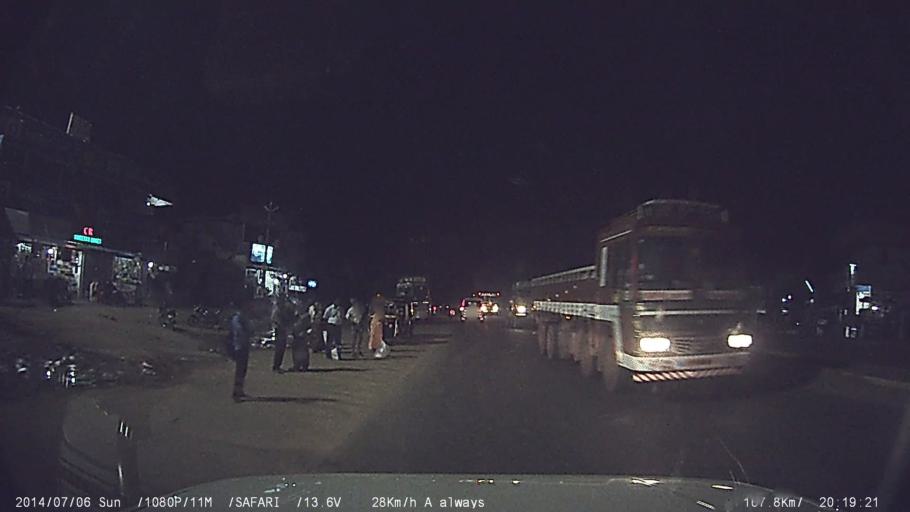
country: IN
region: Kerala
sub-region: Palakkad district
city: Palakkad
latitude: 10.7782
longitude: 76.7113
